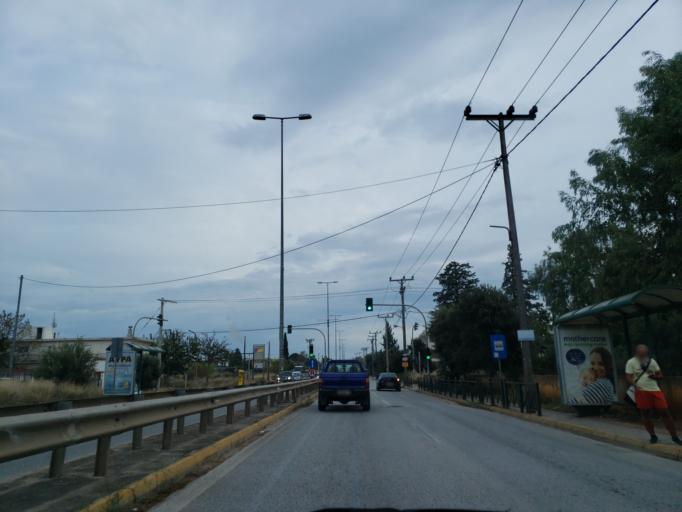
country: GR
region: Attica
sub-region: Nomarchia Anatolikis Attikis
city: Nea Makri
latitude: 38.0995
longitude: 23.9712
